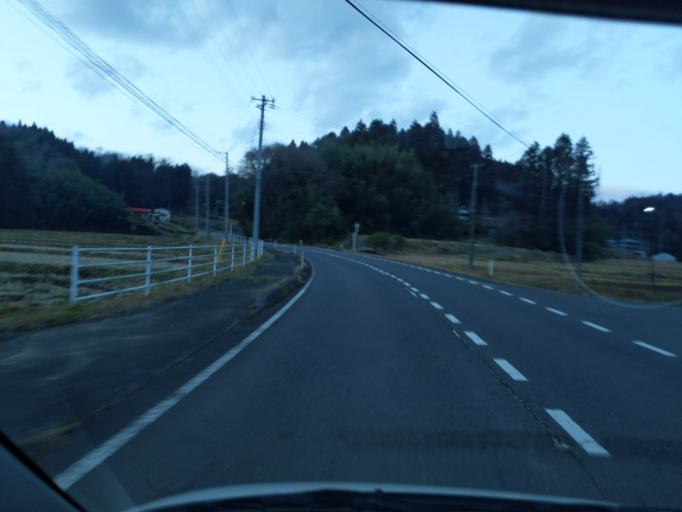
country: JP
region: Iwate
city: Ichinoseki
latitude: 38.8107
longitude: 141.1173
